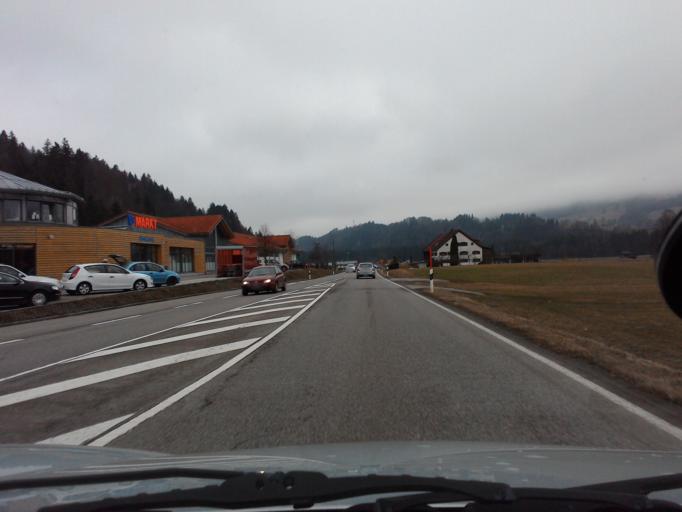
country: DE
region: Bavaria
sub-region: Swabia
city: Oberstdorf
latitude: 47.4316
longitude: 10.2694
